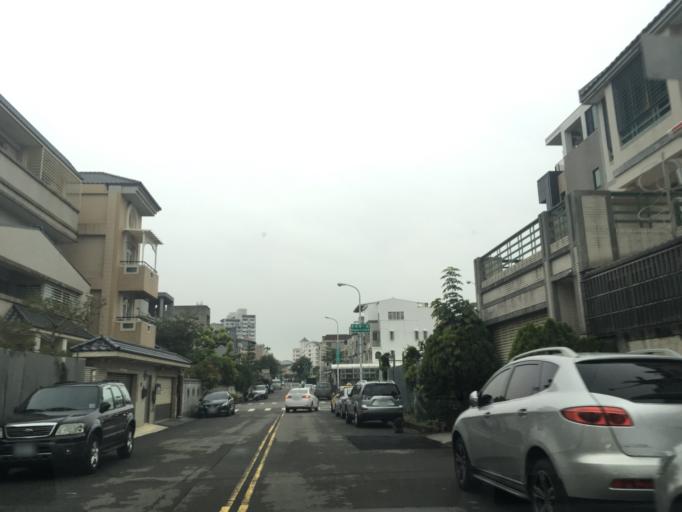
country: TW
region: Taiwan
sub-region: Taichung City
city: Taichung
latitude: 24.1655
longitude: 120.7086
